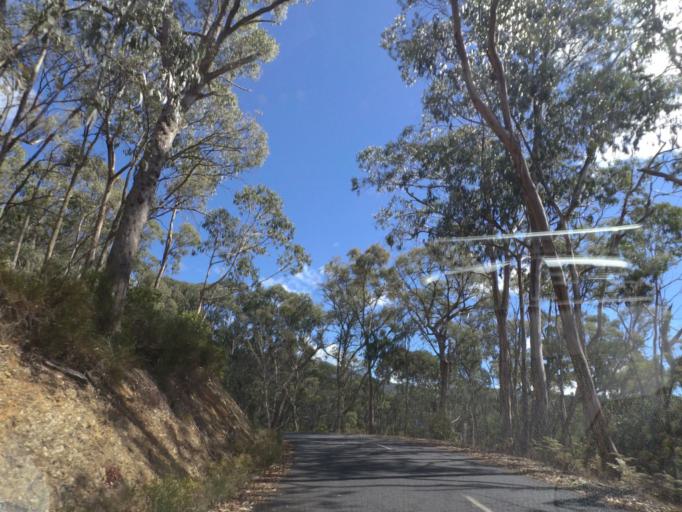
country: AU
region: Victoria
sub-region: Murrindindi
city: Alexandra
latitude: -37.3363
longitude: 145.9601
